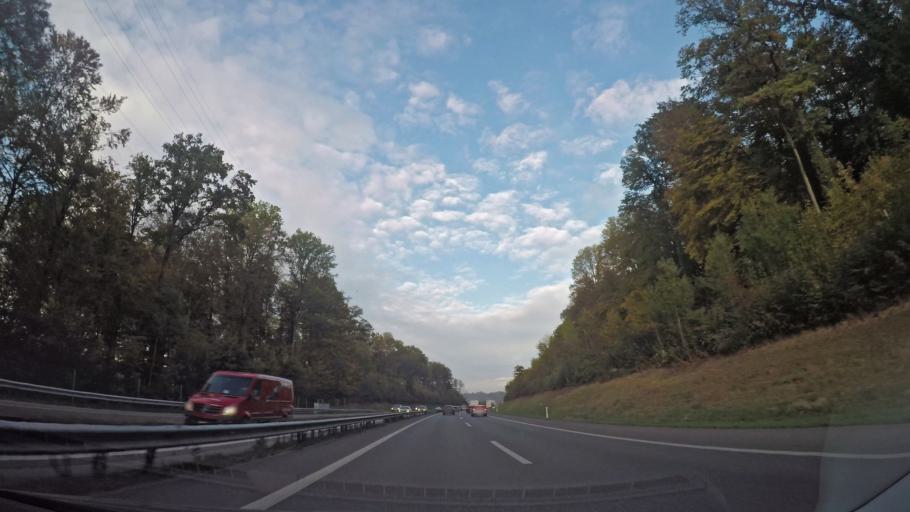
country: CH
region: Aargau
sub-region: Bezirk Aarau
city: Suhr
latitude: 47.3615
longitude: 8.0690
